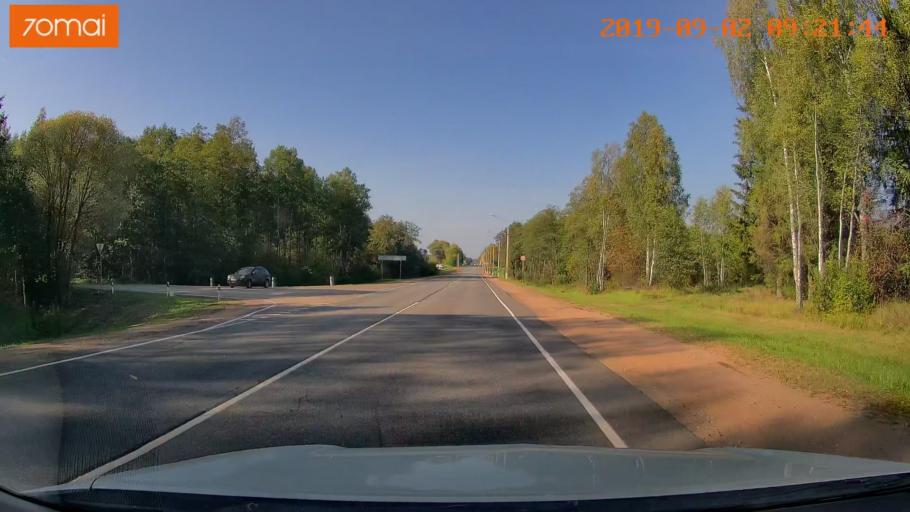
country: RU
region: Kaluga
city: Yukhnov
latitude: 54.7895
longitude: 35.3525
